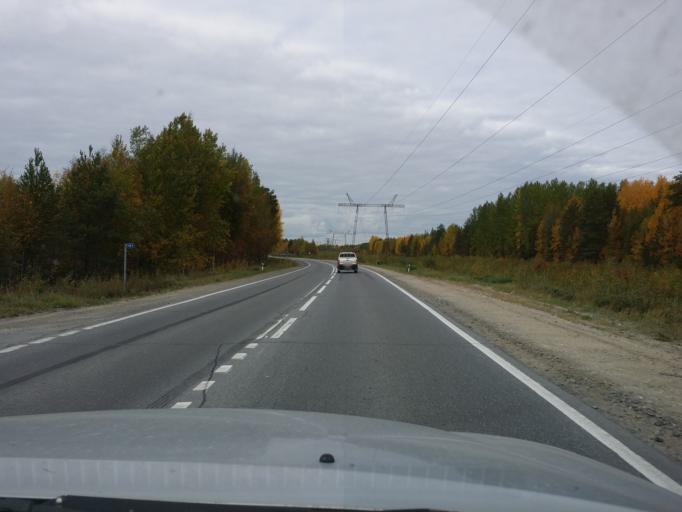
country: RU
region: Khanty-Mansiyskiy Avtonomnyy Okrug
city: Megion
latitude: 61.1595
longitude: 75.7274
